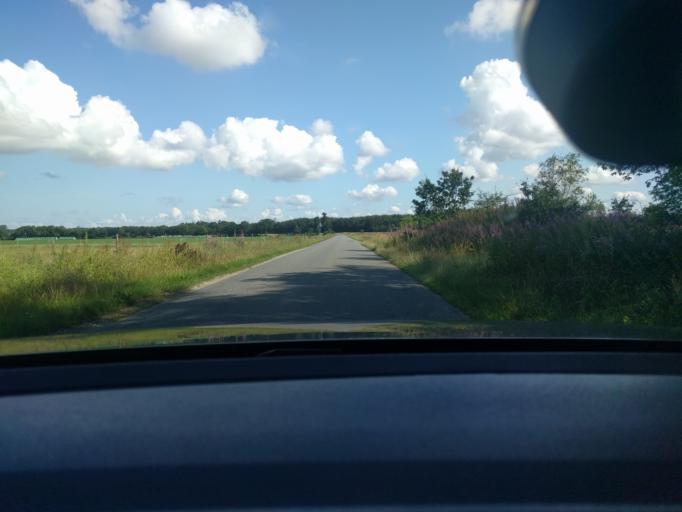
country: DK
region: Central Jutland
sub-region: Viborg Kommune
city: Viborg
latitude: 56.4324
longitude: 9.3128
